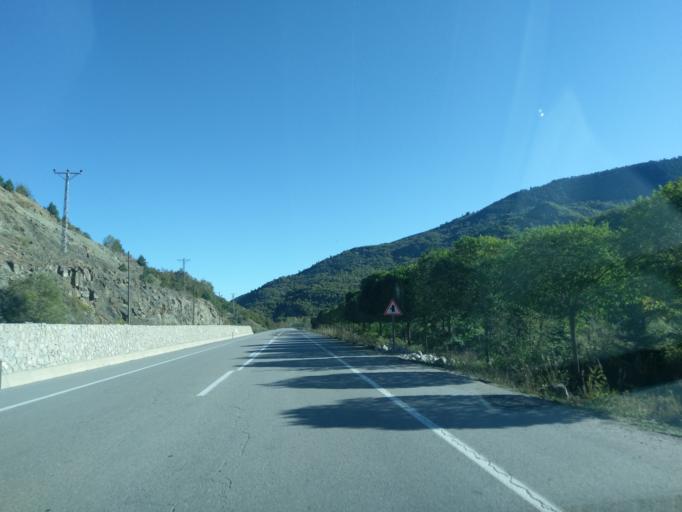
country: TR
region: Sinop
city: Erfelek
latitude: 41.7269
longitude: 34.9444
